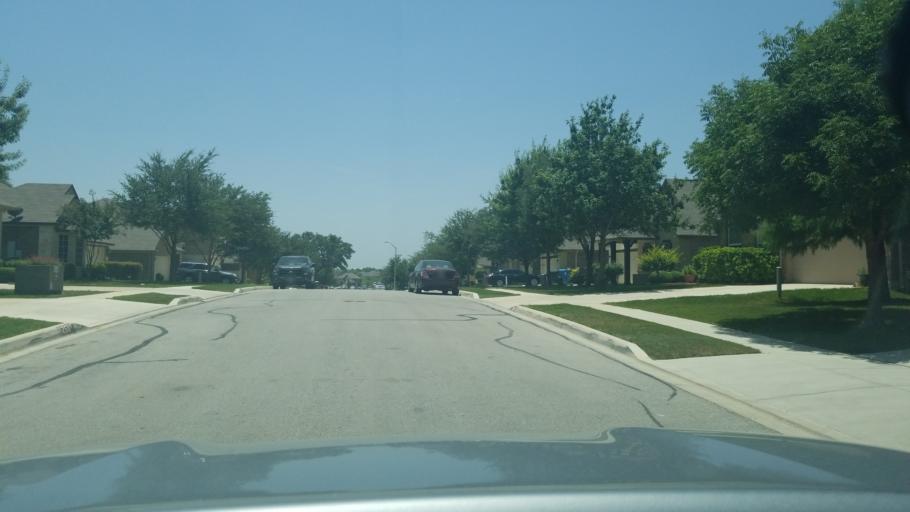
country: US
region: Texas
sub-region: Guadalupe County
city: Cibolo
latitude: 29.5803
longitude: -98.2279
